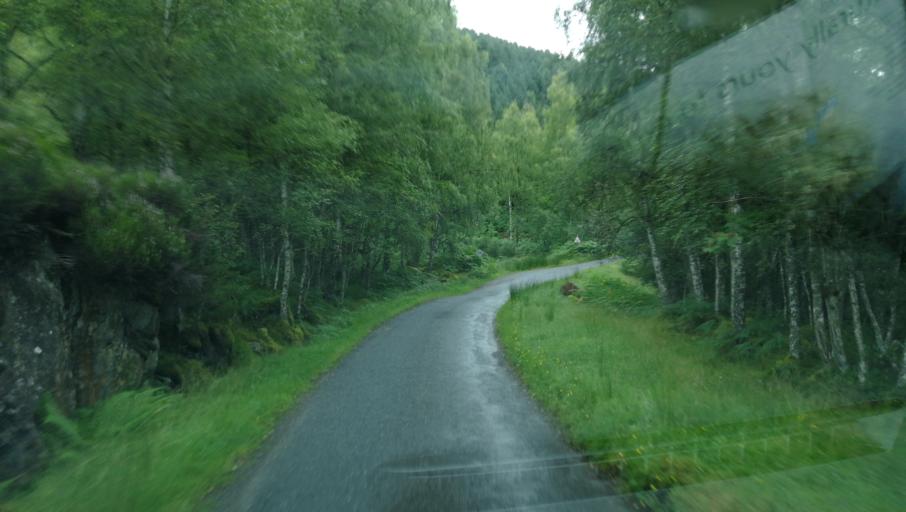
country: GB
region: Scotland
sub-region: Highland
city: Spean Bridge
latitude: 57.2931
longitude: -4.9176
